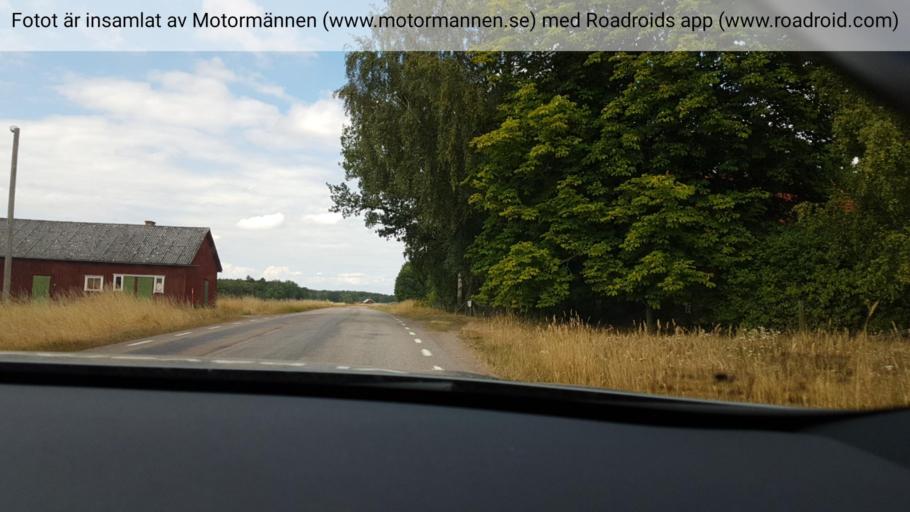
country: SE
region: Vaestra Goetaland
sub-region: Lidkopings Kommun
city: Vinninga
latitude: 58.4310
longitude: 13.3454
